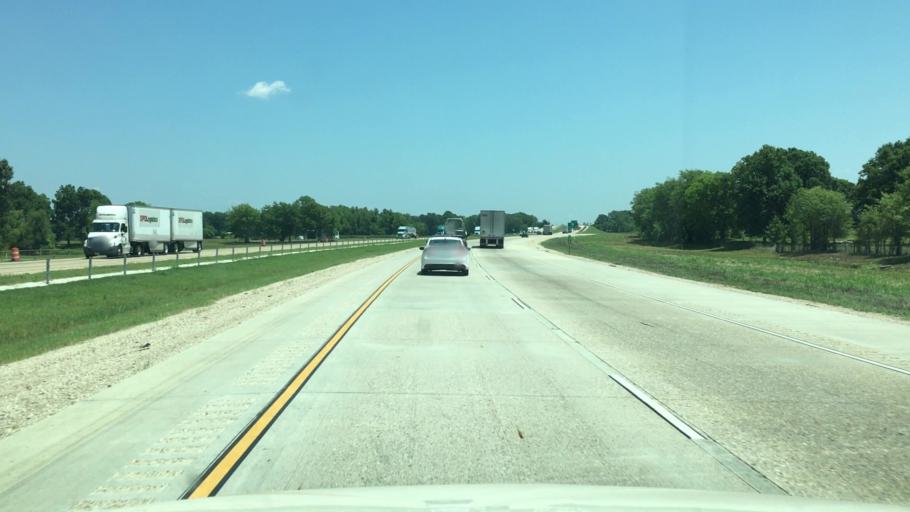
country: US
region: Arkansas
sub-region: Miller County
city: Texarkana
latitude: 33.5477
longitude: -93.8839
